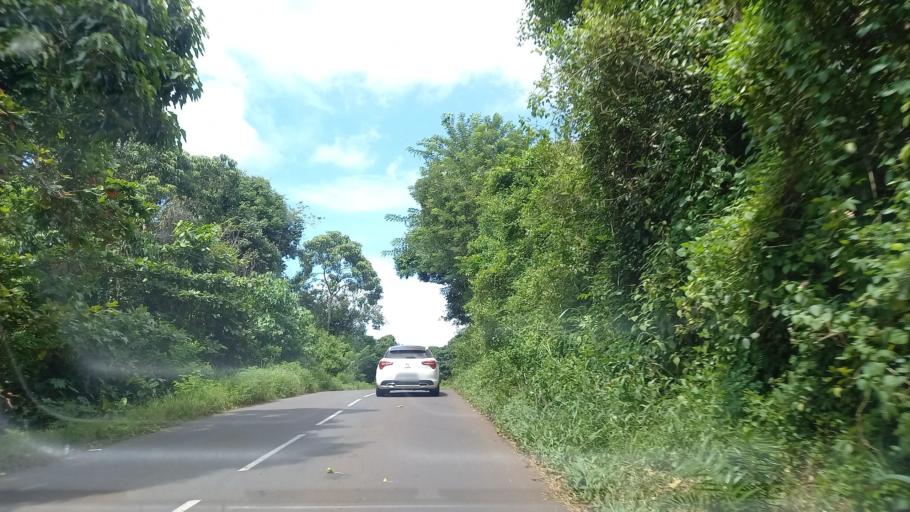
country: YT
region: Dembeni
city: Dembeni
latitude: -12.7881
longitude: 45.1643
